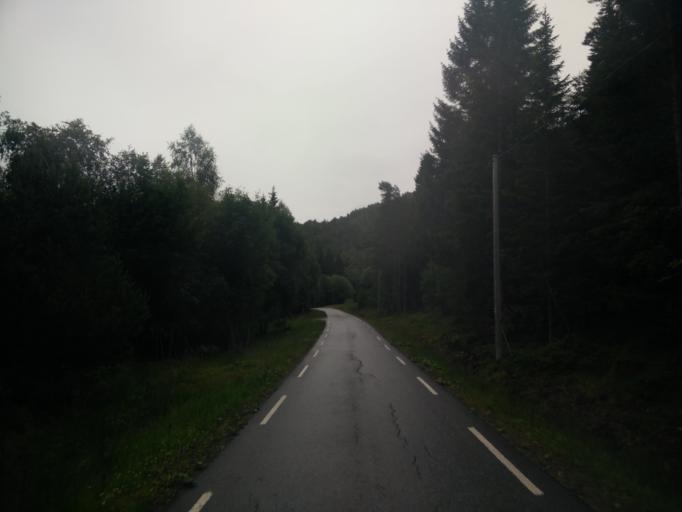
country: NO
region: More og Romsdal
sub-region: Kristiansund
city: Rensvik
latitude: 63.0280
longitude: 7.9049
